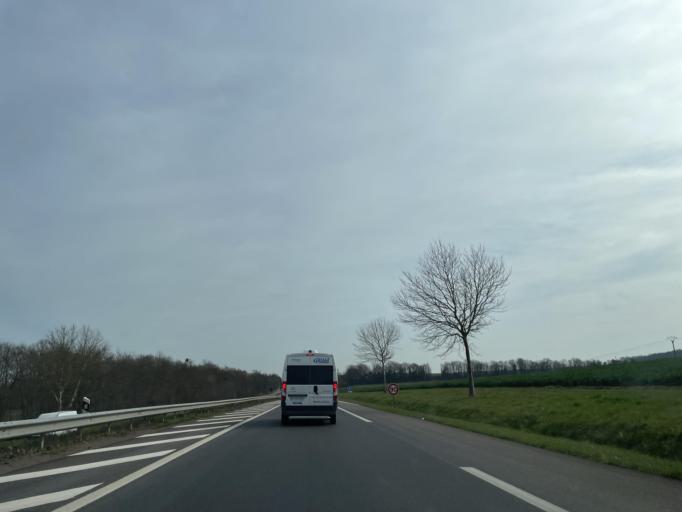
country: FR
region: Champagne-Ardenne
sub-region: Departement de l'Aube
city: Villenauxe-la-Grande
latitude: 48.5085
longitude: 3.5875
